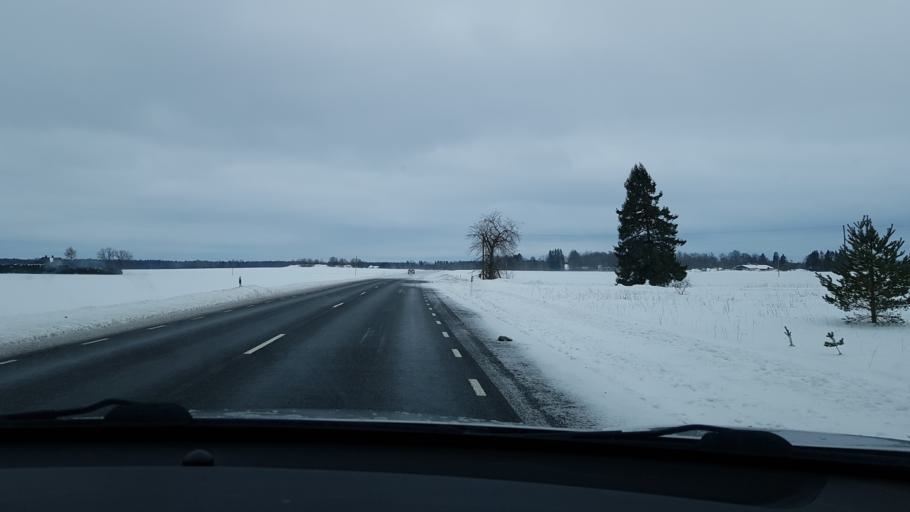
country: EE
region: Jaervamaa
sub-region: Jaerva-Jaani vald
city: Jarva-Jaani
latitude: 59.0898
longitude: 25.8326
